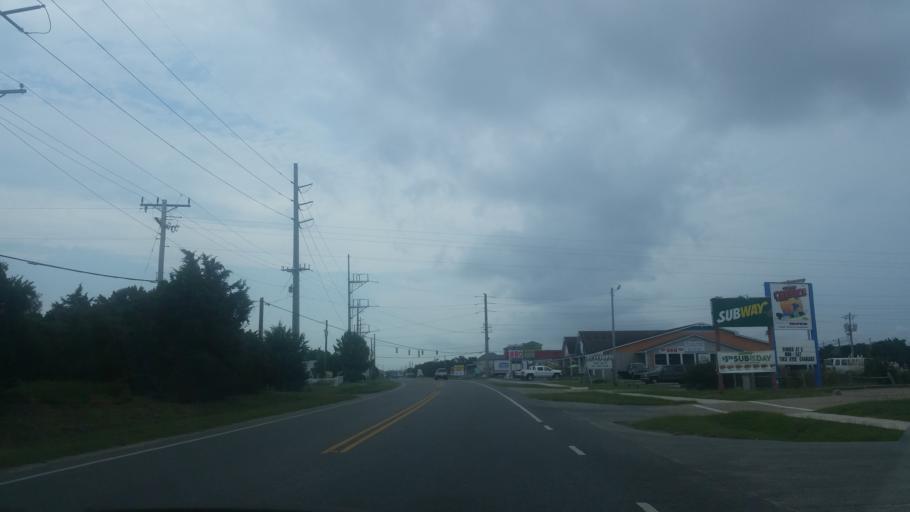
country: US
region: North Carolina
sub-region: Dare County
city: Buxton
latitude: 35.3538
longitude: -75.5030
